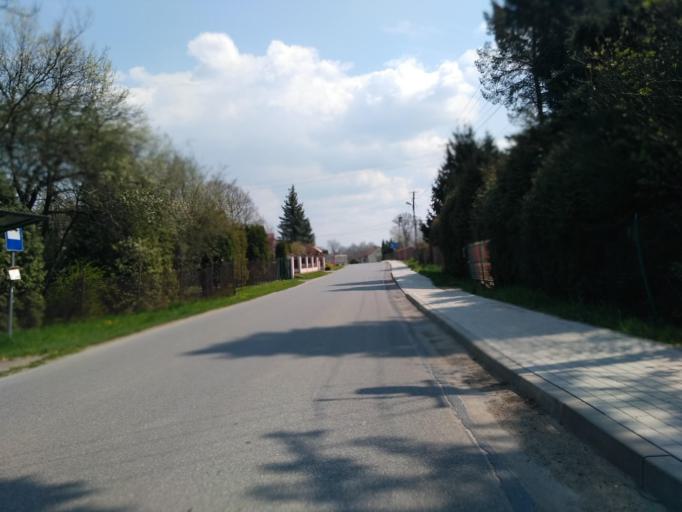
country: PL
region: Subcarpathian Voivodeship
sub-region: Powiat jasielski
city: Tarnowiec
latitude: 49.7387
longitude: 21.5381
